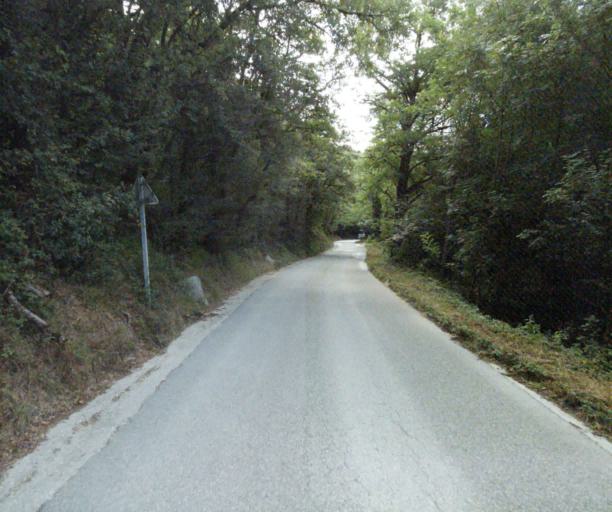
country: FR
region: Midi-Pyrenees
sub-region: Departement du Tarn
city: Soreze
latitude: 43.4609
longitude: 2.1059
